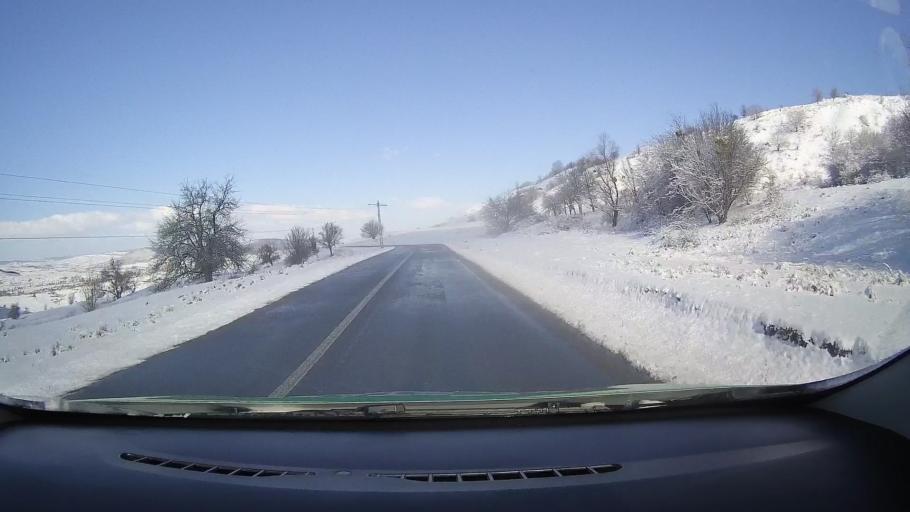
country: RO
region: Sibiu
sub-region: Comuna Avrig
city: Avrig
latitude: 45.7831
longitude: 24.3746
